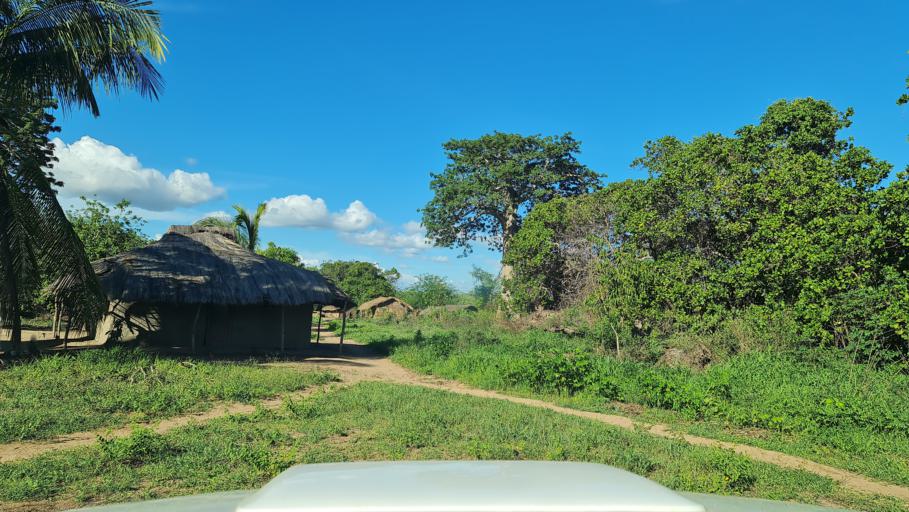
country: MZ
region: Nampula
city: Ilha de Mocambique
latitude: -15.2448
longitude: 40.1797
